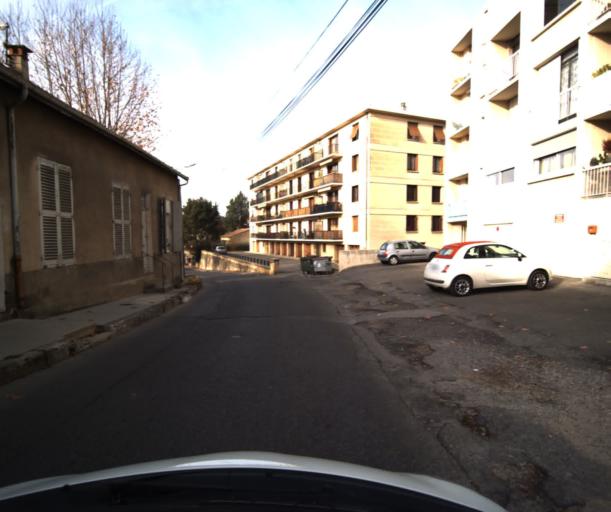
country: FR
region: Provence-Alpes-Cote d'Azur
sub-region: Departement du Vaucluse
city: Pertuis
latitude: 43.6898
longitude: 5.4984
